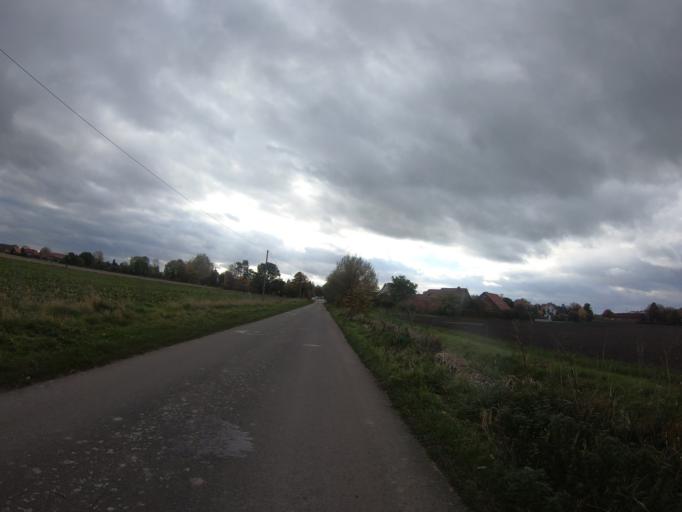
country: DE
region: Lower Saxony
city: Adenbuettel
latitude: 52.3811
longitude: 10.4840
